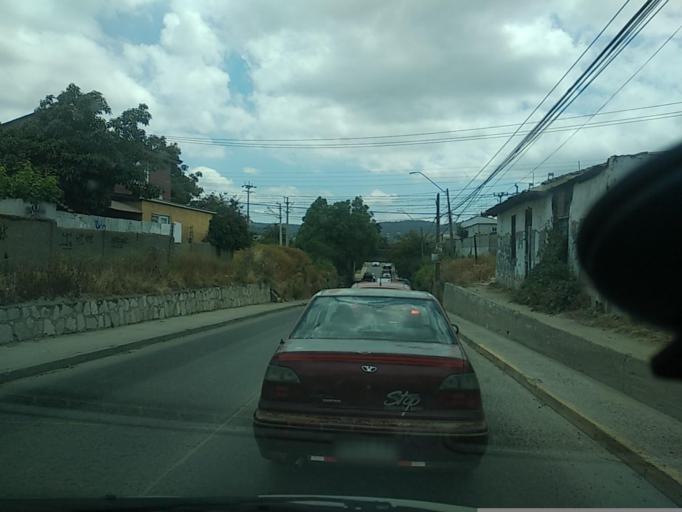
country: CL
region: Valparaiso
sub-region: Provincia de Marga Marga
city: Villa Alemana
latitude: -33.0443
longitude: -71.4053
